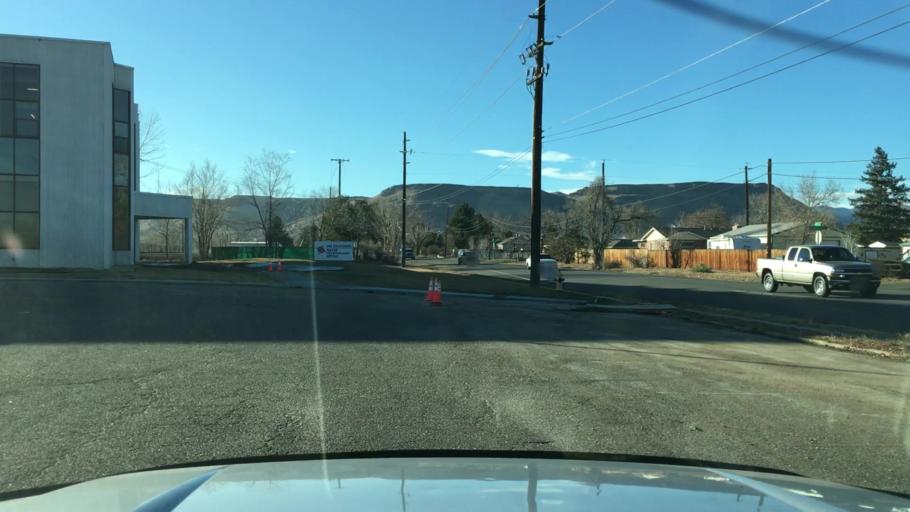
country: US
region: Colorado
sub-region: Jefferson County
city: Applewood
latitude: 39.7760
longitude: -105.1611
